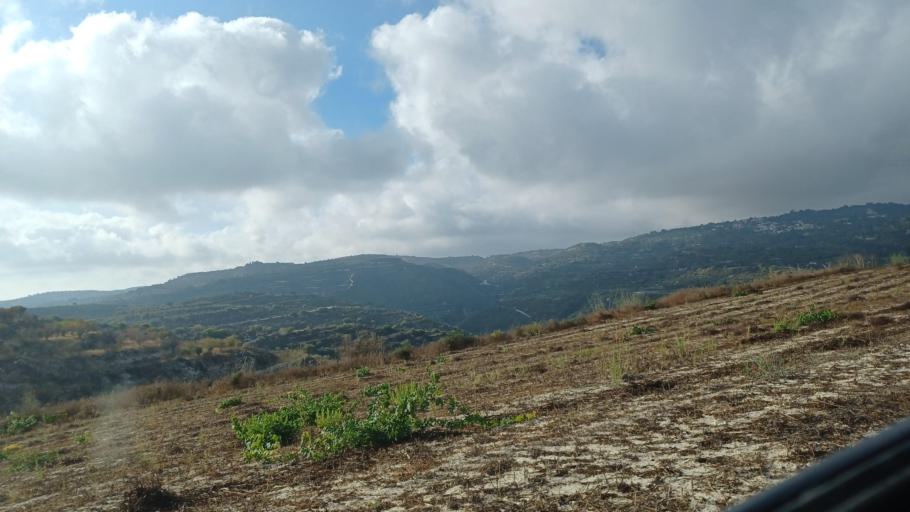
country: CY
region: Pafos
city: Tala
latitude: 34.8797
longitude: 32.4565
